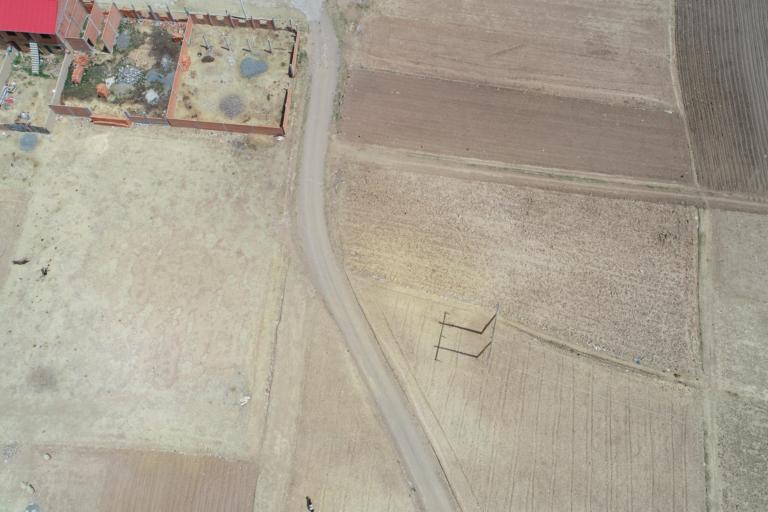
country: BO
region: La Paz
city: Achacachi
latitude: -15.9133
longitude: -68.8849
